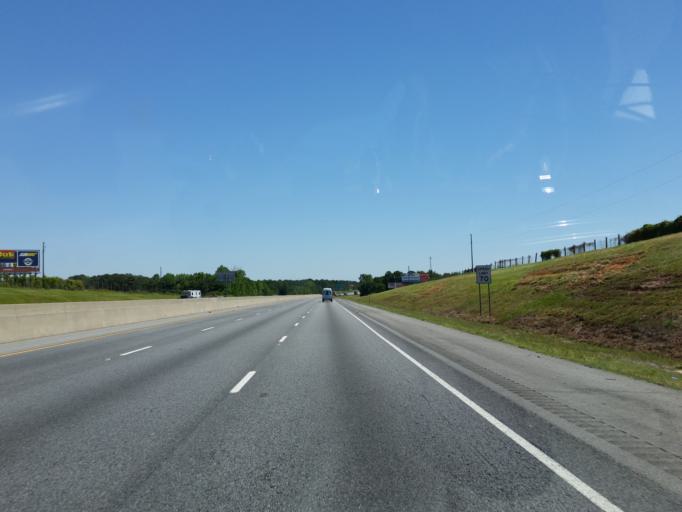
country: US
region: Georgia
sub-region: Tift County
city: Tifton
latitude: 31.5637
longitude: -83.5429
